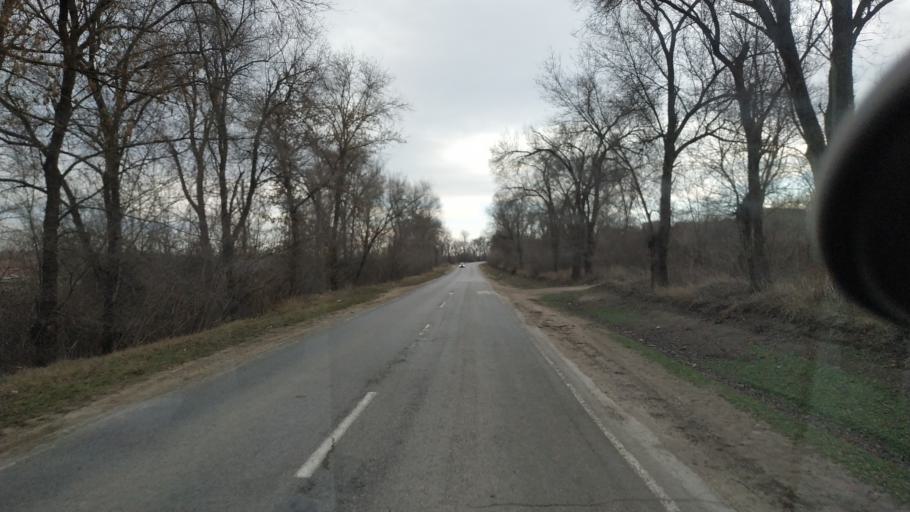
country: MD
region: Chisinau
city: Vadul lui Voda
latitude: 47.1285
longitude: 29.0627
